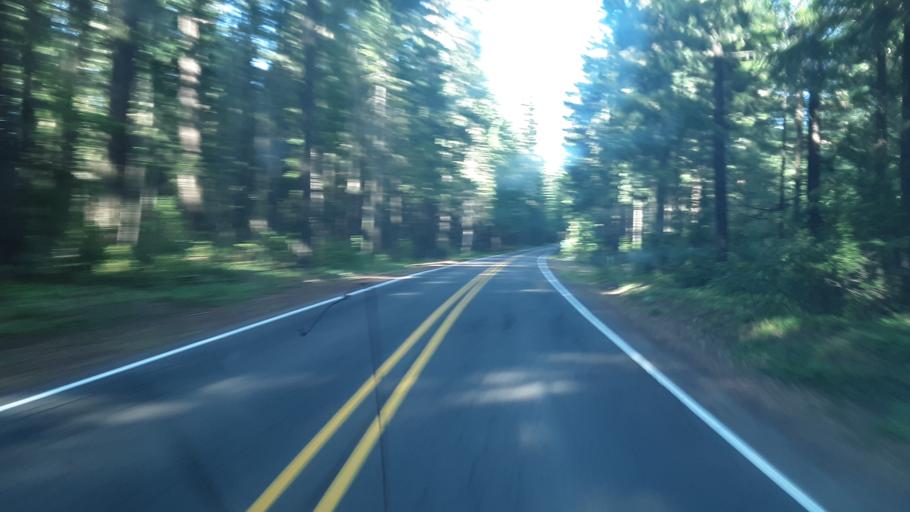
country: US
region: Oregon
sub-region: Jackson County
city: Shady Cove
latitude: 42.9492
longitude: -122.4103
